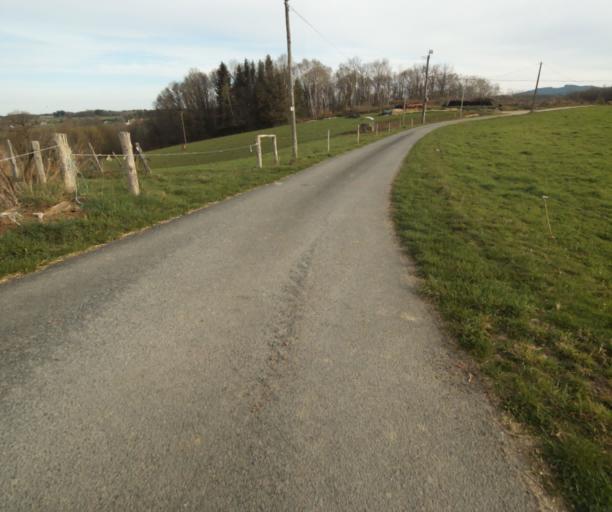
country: FR
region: Limousin
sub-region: Departement de la Correze
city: Chamboulive
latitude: 45.4592
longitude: 1.7574
